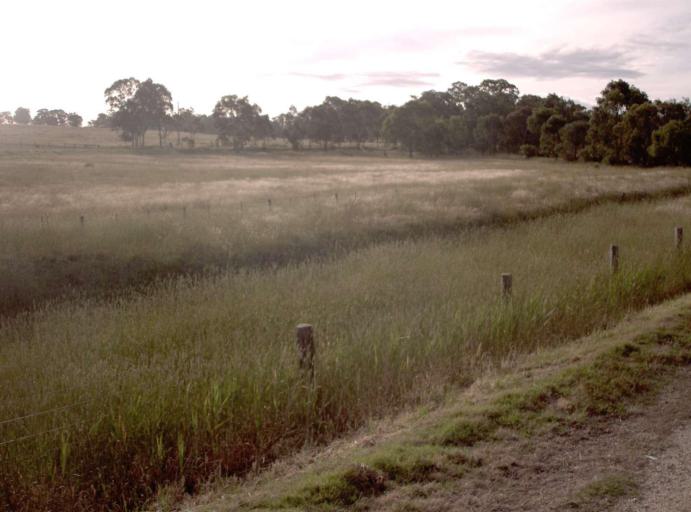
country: AU
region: Victoria
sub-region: Wellington
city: Sale
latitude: -37.9143
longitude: 146.9976
